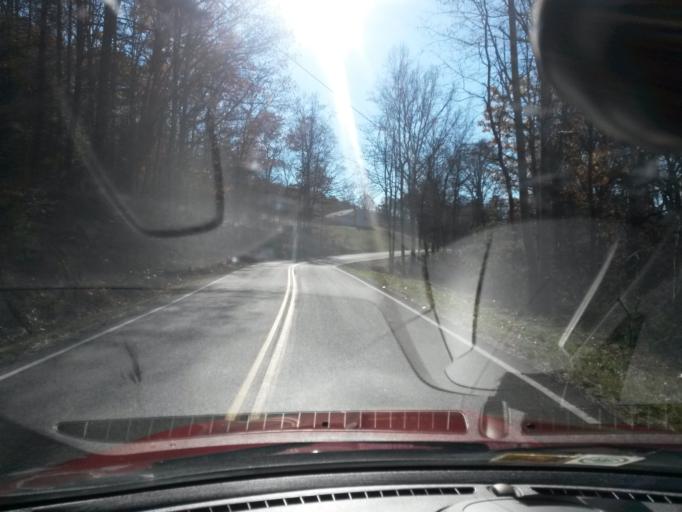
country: US
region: Virginia
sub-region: Botetourt County
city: Buchanan
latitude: 37.6085
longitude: -79.7358
